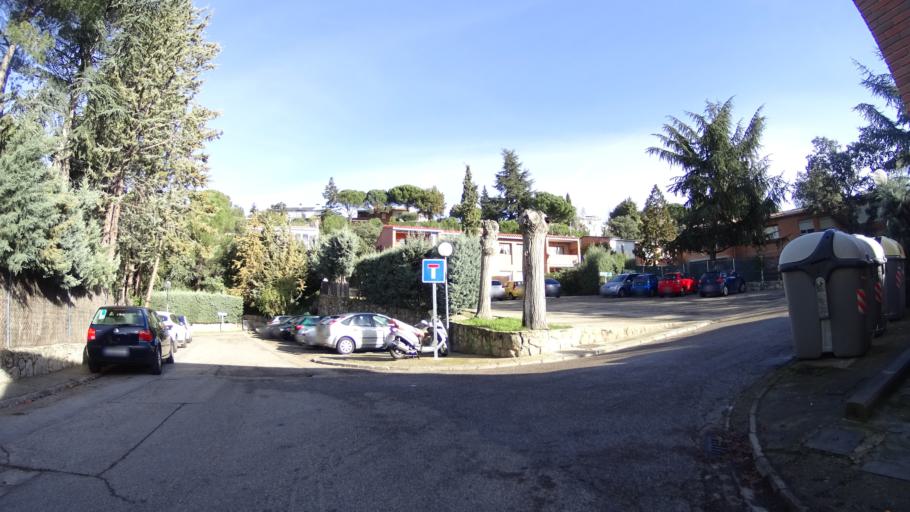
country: ES
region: Madrid
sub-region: Provincia de Madrid
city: Hoyo de Manzanares
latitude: 40.6122
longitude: -3.9443
